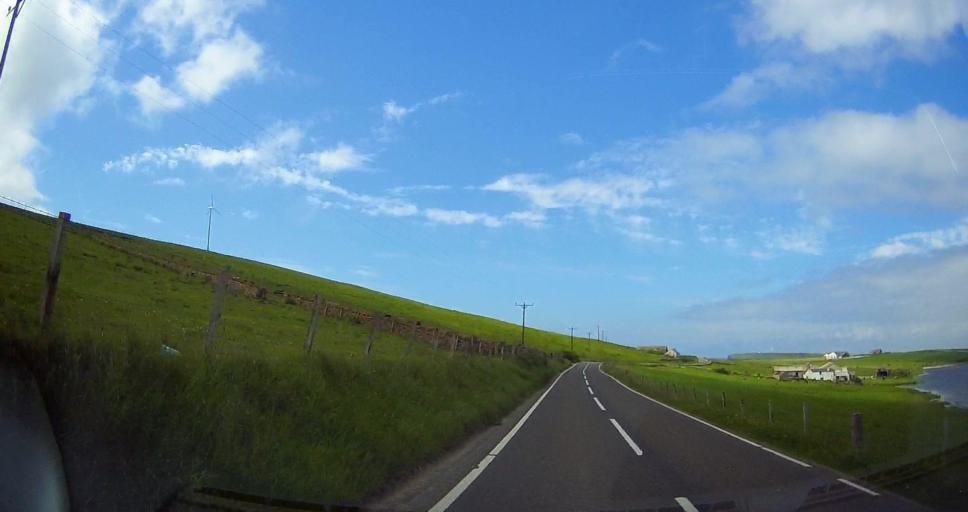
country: GB
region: Scotland
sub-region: Orkney Islands
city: Stromness
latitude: 59.1139
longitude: -3.2983
